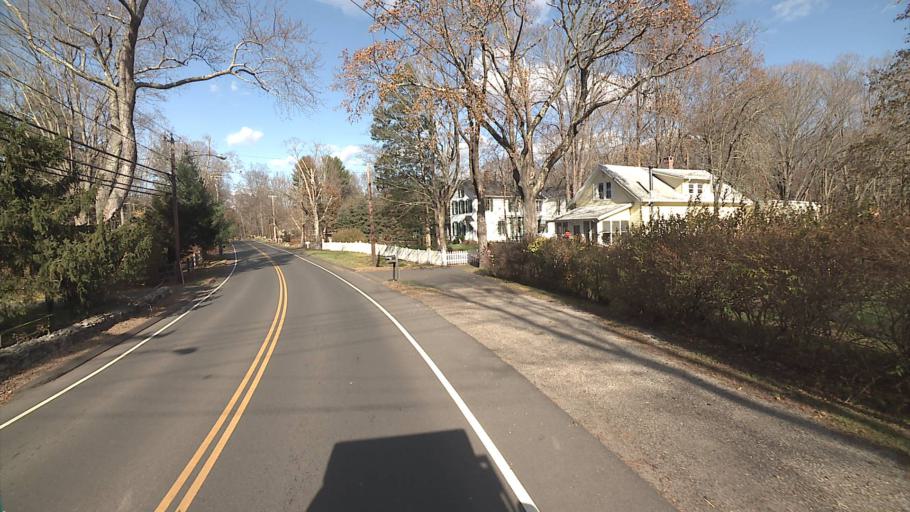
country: US
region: Connecticut
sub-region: Fairfield County
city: Westport
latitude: 41.1522
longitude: -73.3929
